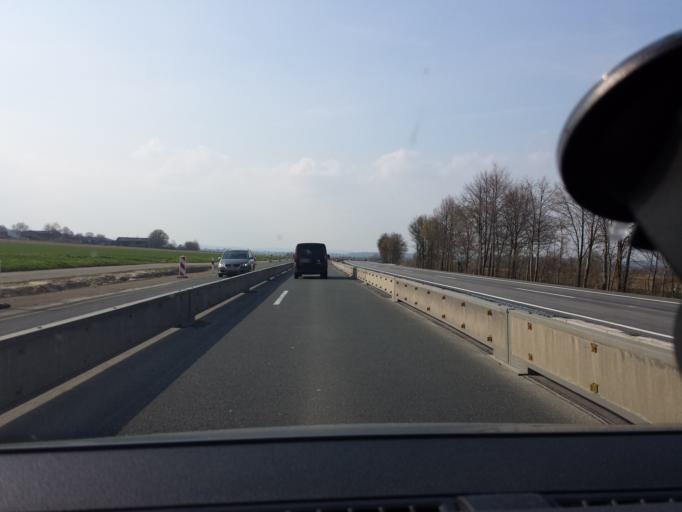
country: DE
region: Lower Saxony
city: Vienenburg
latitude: 51.9696
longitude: 10.5683
